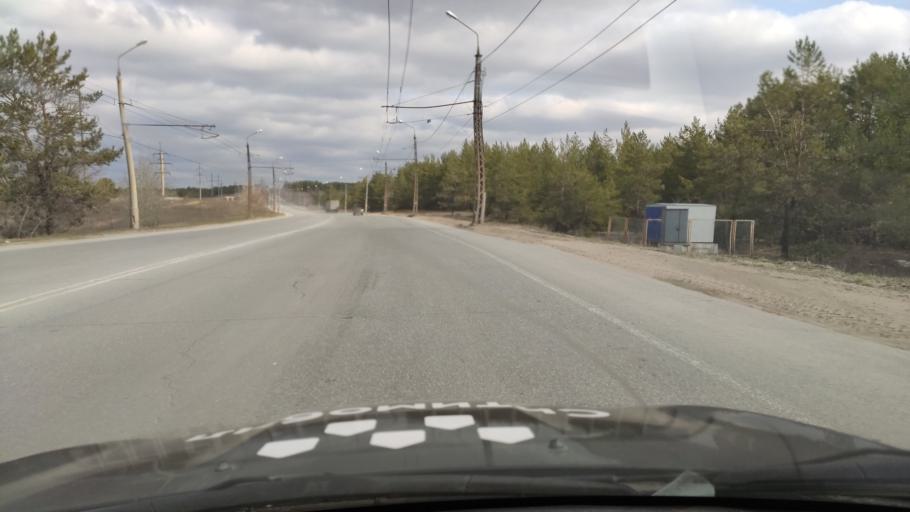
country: RU
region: Samara
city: Zhigulevsk
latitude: 53.4996
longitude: 49.5123
